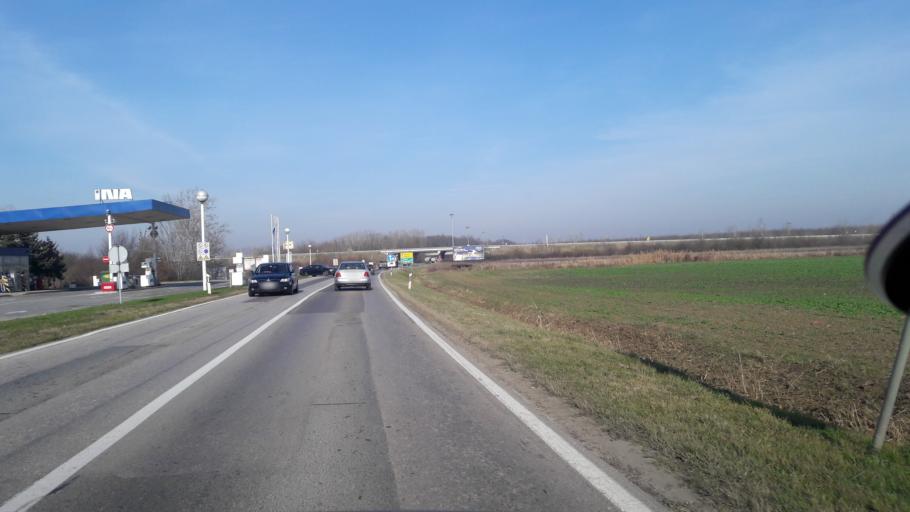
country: HR
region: Vukovarsko-Srijemska
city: Zupanja
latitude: 45.1022
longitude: 18.7008
